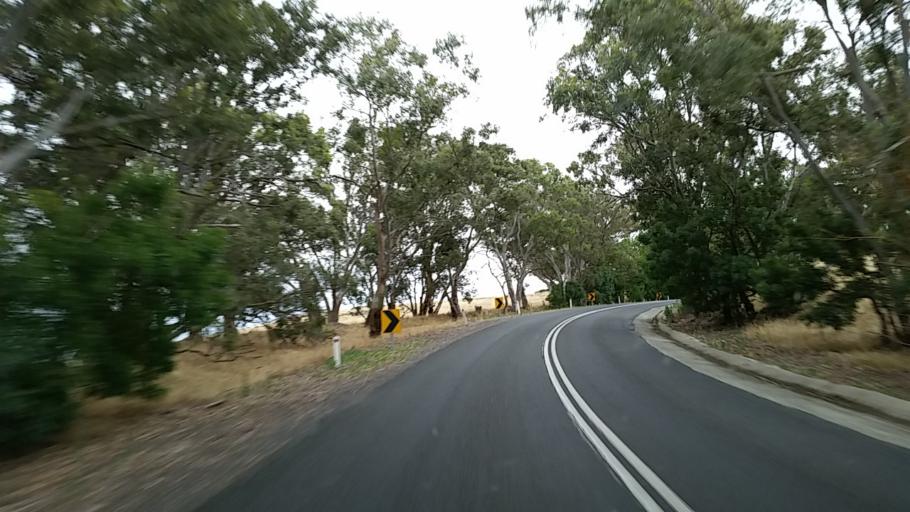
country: AU
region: South Australia
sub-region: Adelaide Hills
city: Birdwood
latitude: -34.7741
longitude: 139.0786
